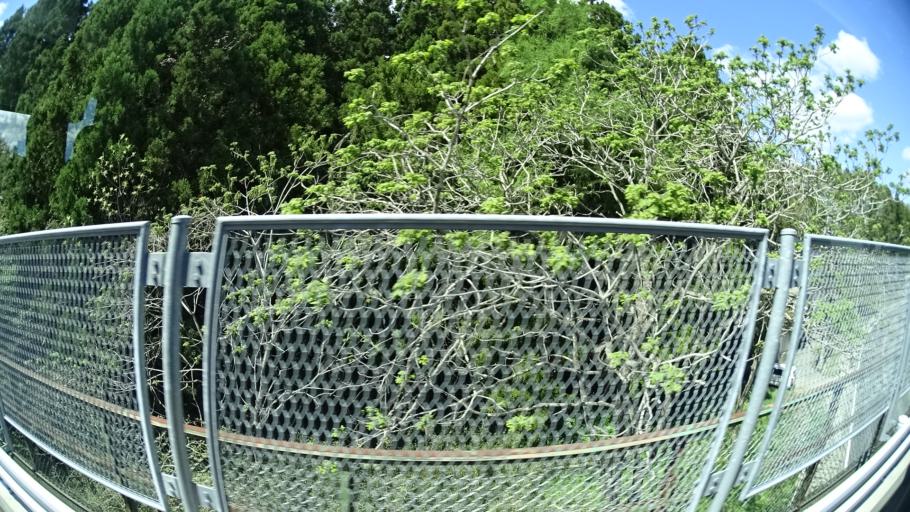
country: JP
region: Miyagi
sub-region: Oshika Gun
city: Onagawa Cho
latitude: 38.6616
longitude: 141.4461
